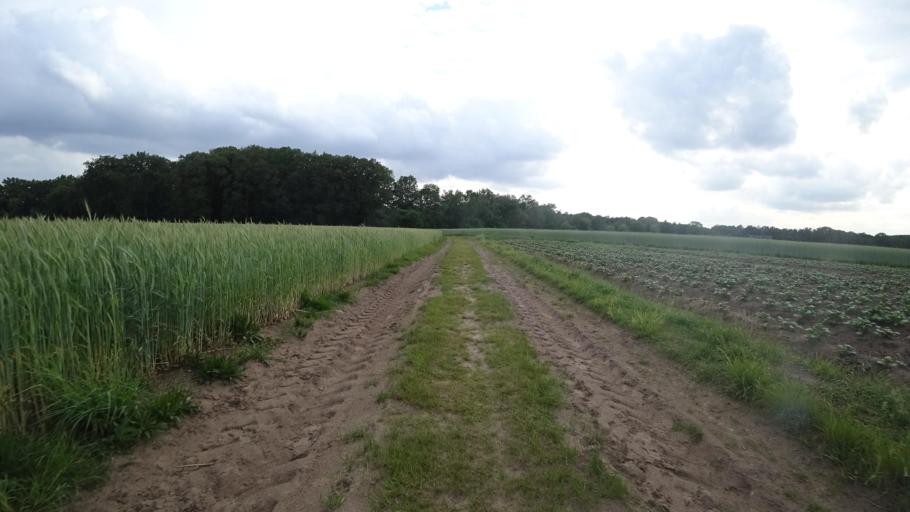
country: DE
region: North Rhine-Westphalia
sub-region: Regierungsbezirk Detmold
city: Guetersloh
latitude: 51.8695
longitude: 8.4133
